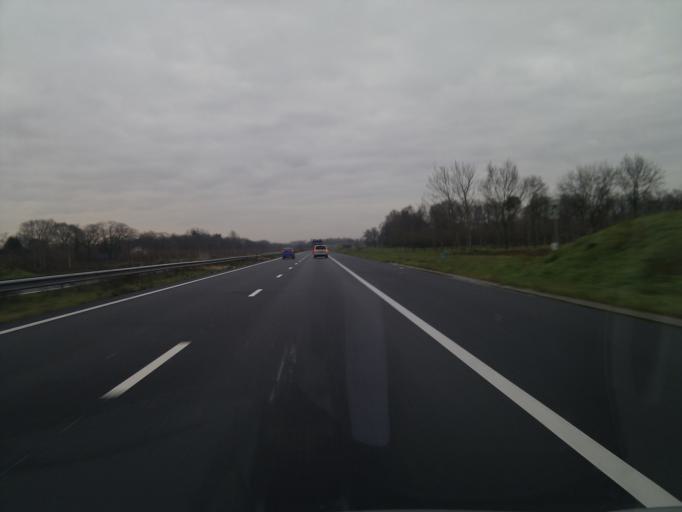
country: NL
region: North Brabant
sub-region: Gemeente Sint-Oedenrode
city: Sint-Oedenrode
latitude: 51.5489
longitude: 5.4802
